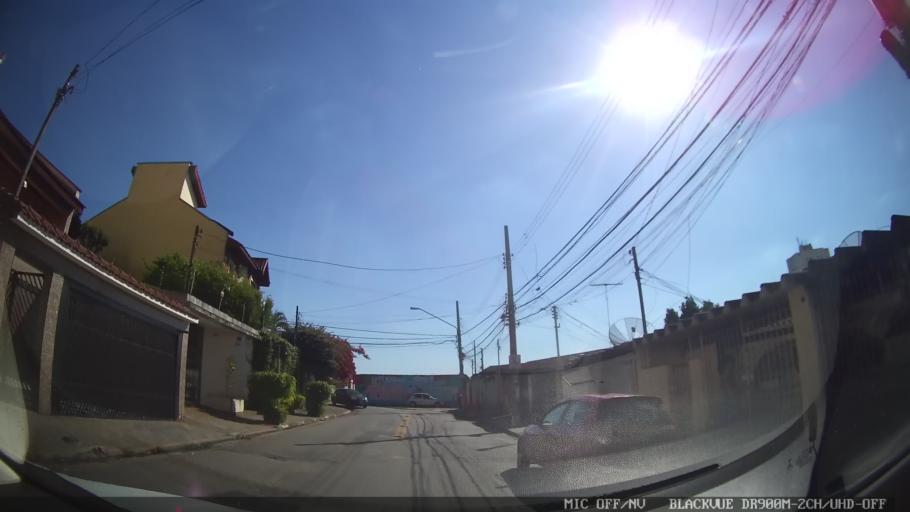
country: BR
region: Sao Paulo
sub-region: Sao Paulo
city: Sao Paulo
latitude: -23.4875
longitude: -46.6438
